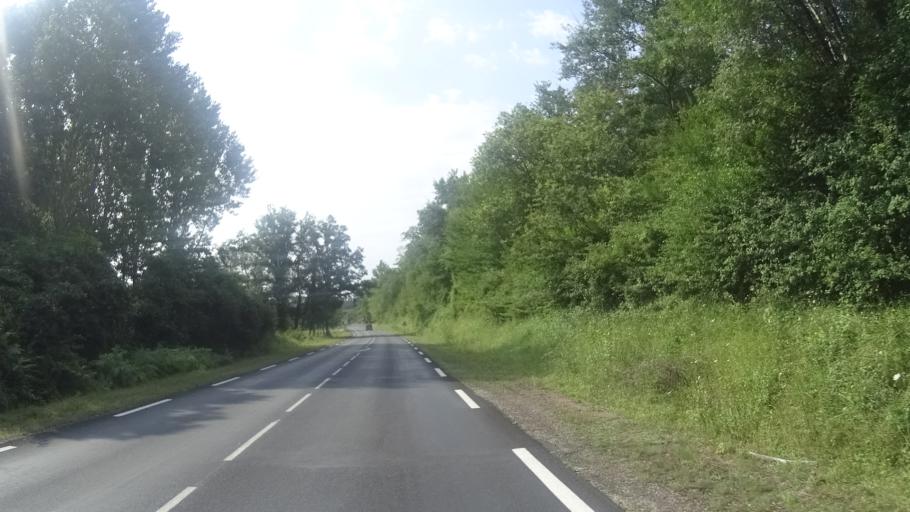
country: FR
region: Aquitaine
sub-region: Departement de la Dordogne
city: Sourzac
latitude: 45.0875
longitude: 0.3817
